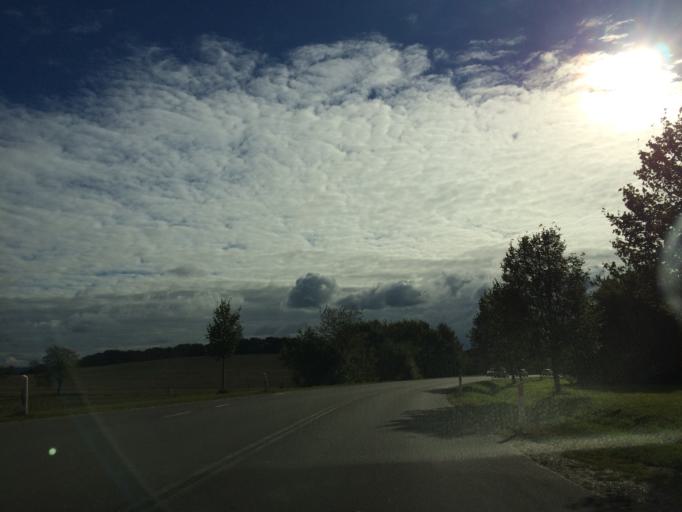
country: DK
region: Central Jutland
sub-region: Skanderborg Kommune
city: Ry
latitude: 56.0805
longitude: 9.7062
